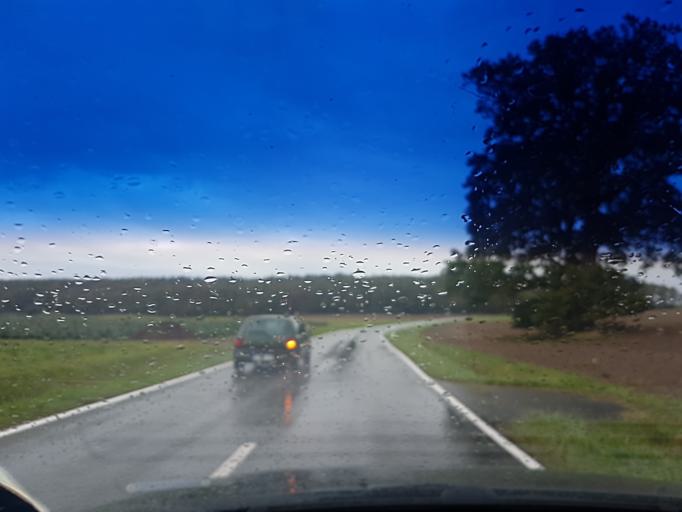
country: DE
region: Bavaria
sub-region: Regierungsbezirk Mittelfranken
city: Wachenroth
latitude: 49.7541
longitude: 10.6662
